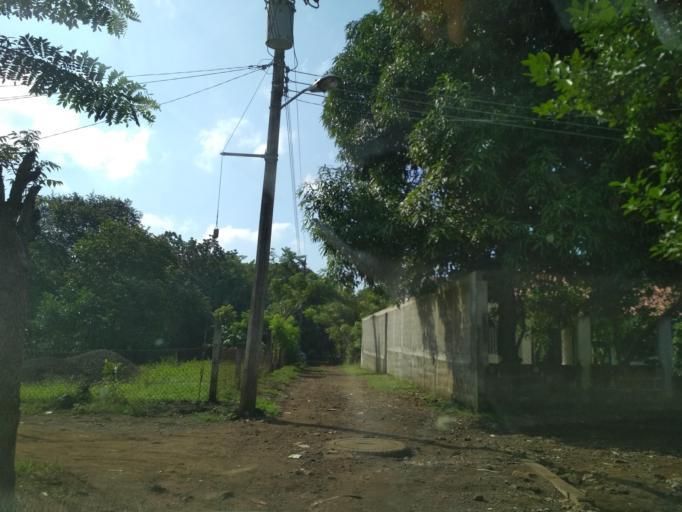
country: MX
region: Veracruz
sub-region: San Andres Tuxtla
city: Matacapan
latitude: 18.4417
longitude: -95.1736
